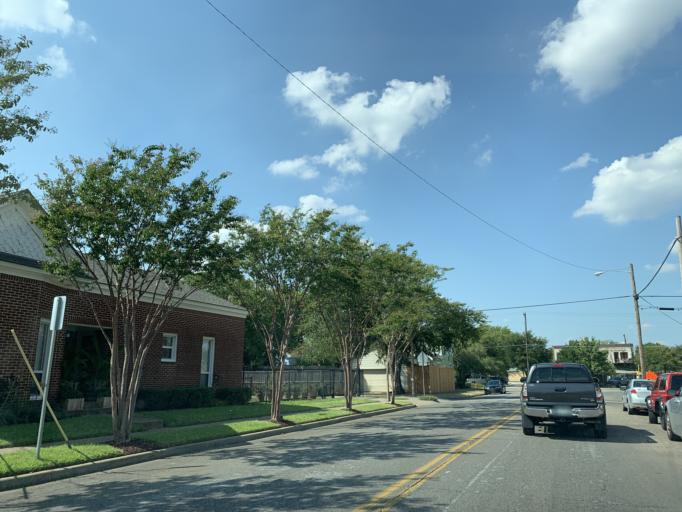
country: US
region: Texas
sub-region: Dallas County
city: Dallas
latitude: 32.7482
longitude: -96.8321
